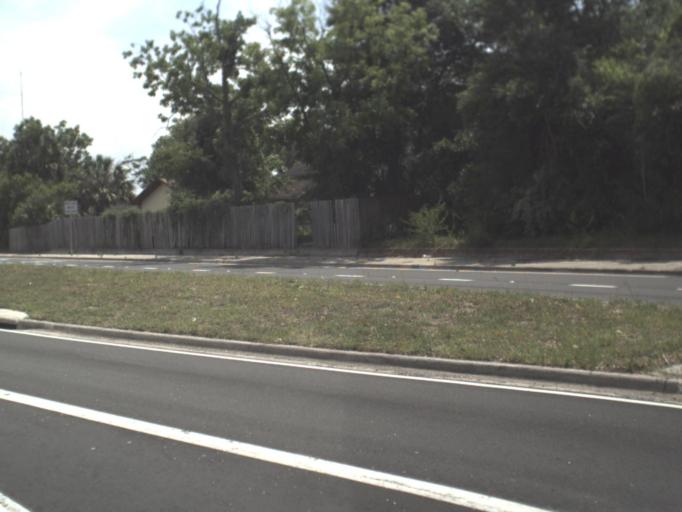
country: US
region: Florida
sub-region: Duval County
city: Jacksonville
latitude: 30.3380
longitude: -81.6368
